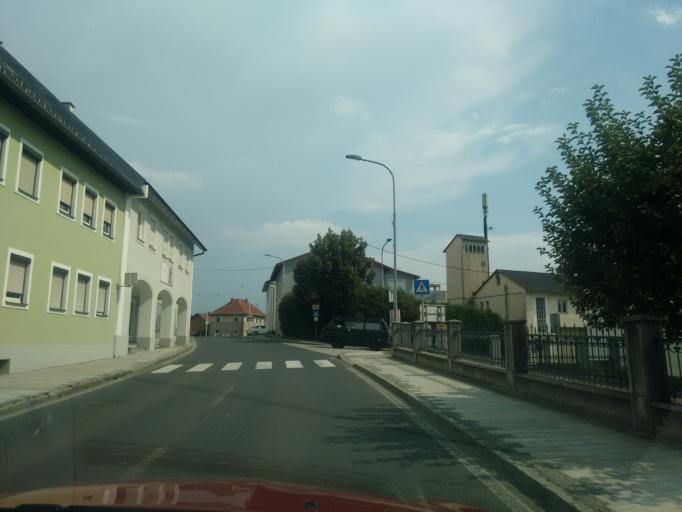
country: AT
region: Upper Austria
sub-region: Politischer Bezirk Grieskirchen
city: Bad Schallerbach
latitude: 48.2638
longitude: 13.9312
